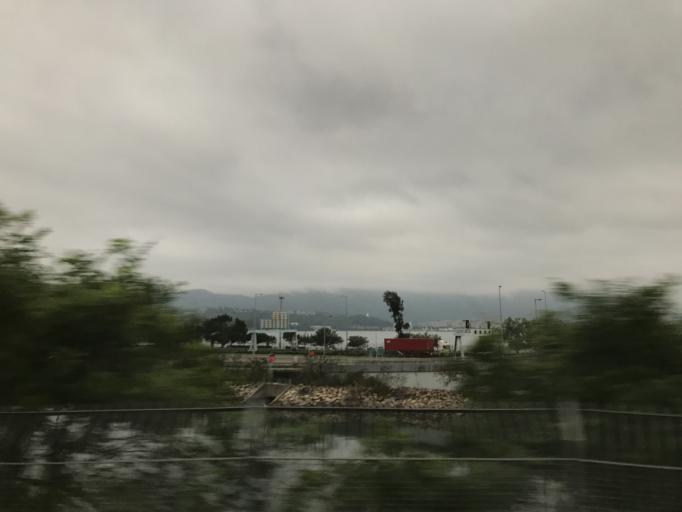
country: HK
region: Tai Po
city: Tai Po
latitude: 22.4368
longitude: 114.1966
